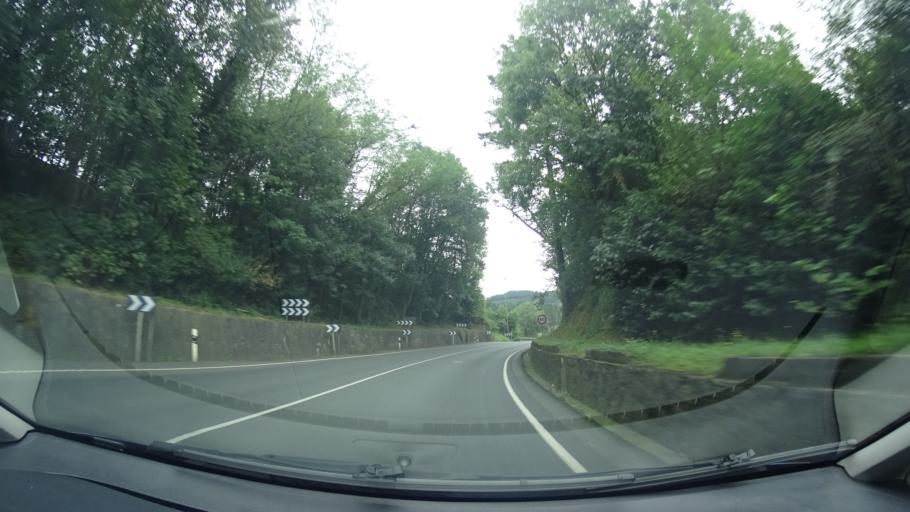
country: ES
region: Basque Country
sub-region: Bizkaia
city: Zeanuri
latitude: 43.1051
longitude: -2.7519
